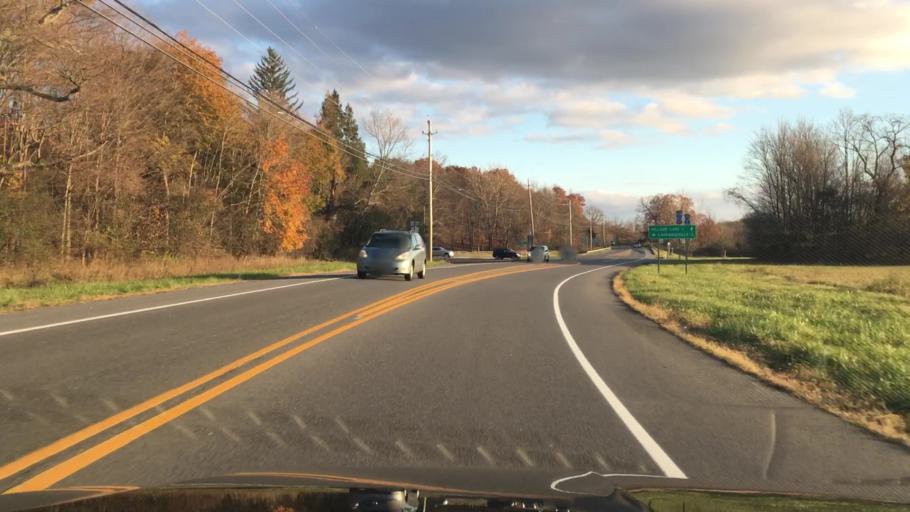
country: US
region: New York
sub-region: Dutchess County
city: Hillside Lake
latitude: 41.6430
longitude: -73.7948
